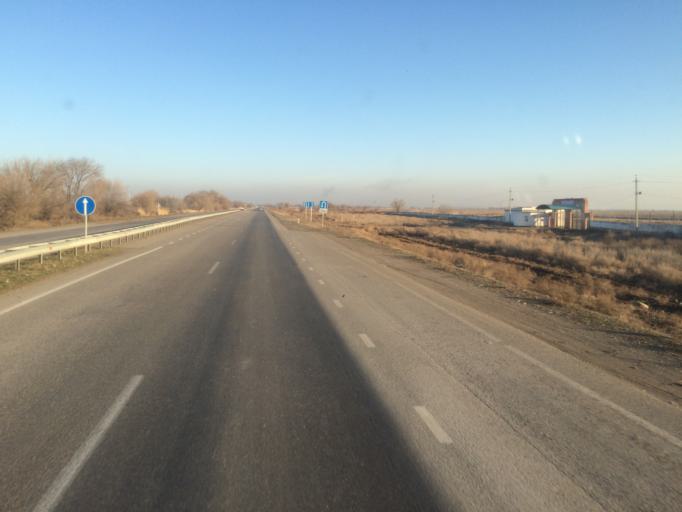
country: KZ
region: Ongtustik Qazaqstan
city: Turkestan
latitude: 43.3505
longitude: 68.1497
